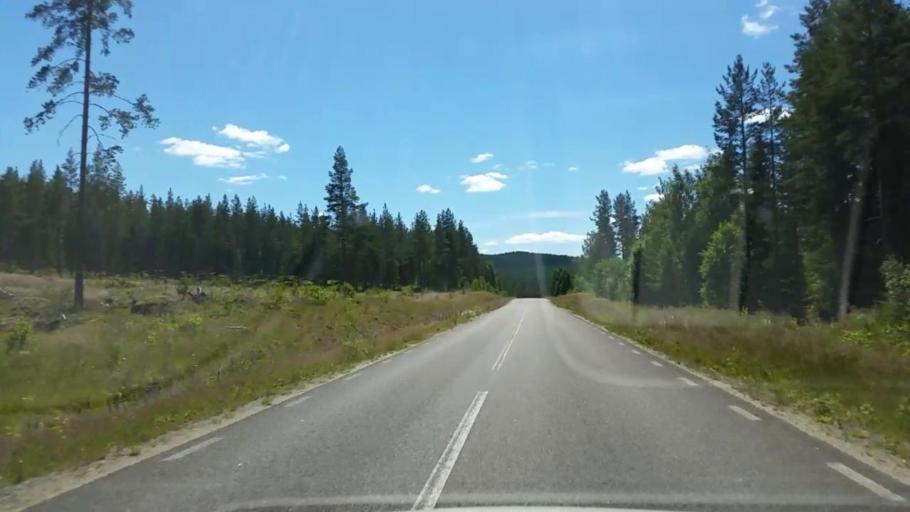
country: SE
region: Gaevleborg
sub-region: Ljusdals Kommun
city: Farila
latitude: 61.6402
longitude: 15.5889
